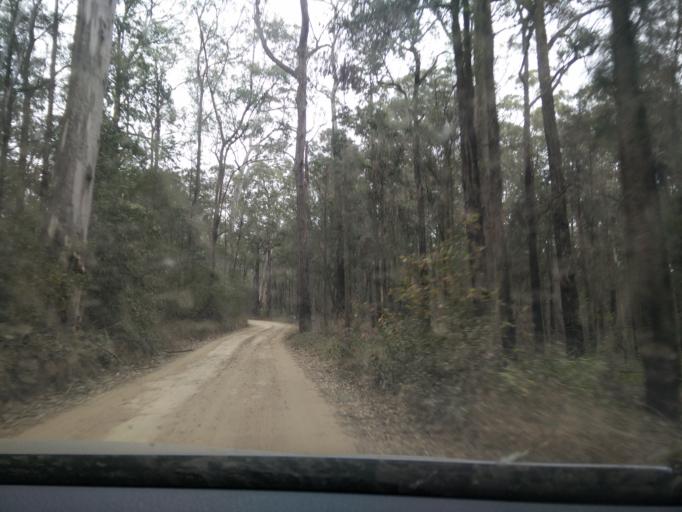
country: AU
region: New South Wales
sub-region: Blue Mountains Municipality
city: Glenbrook
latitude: -33.8291
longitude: 150.5727
